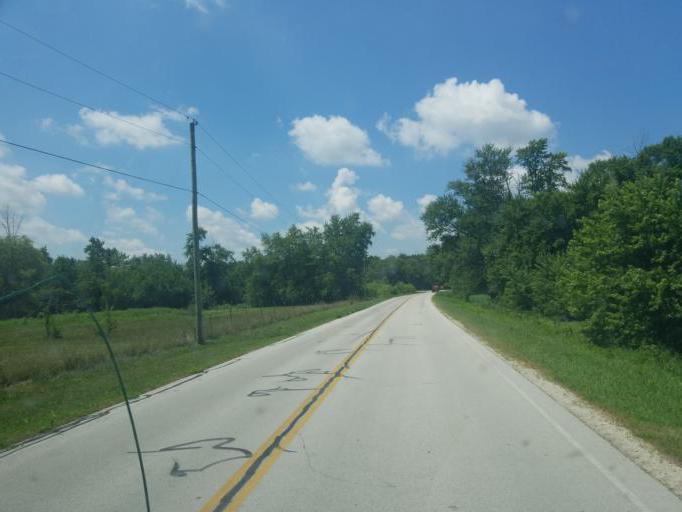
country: US
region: Ohio
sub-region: Mercer County
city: Rockford
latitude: 40.6784
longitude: -84.5154
